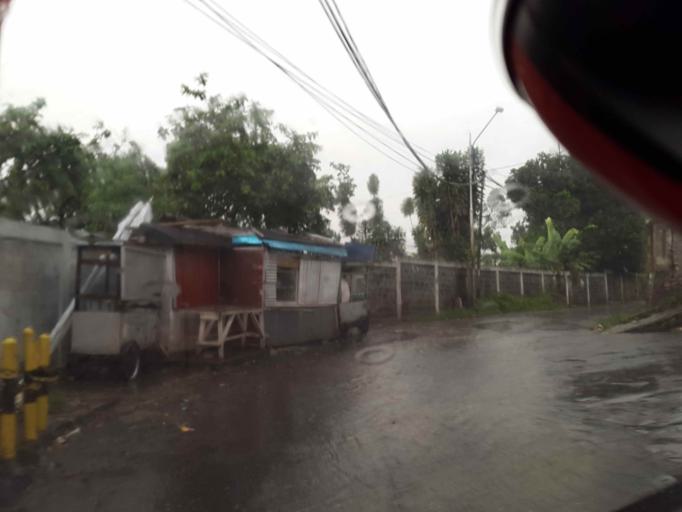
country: ID
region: West Java
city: Sukabumi
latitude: -6.9044
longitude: 106.9294
